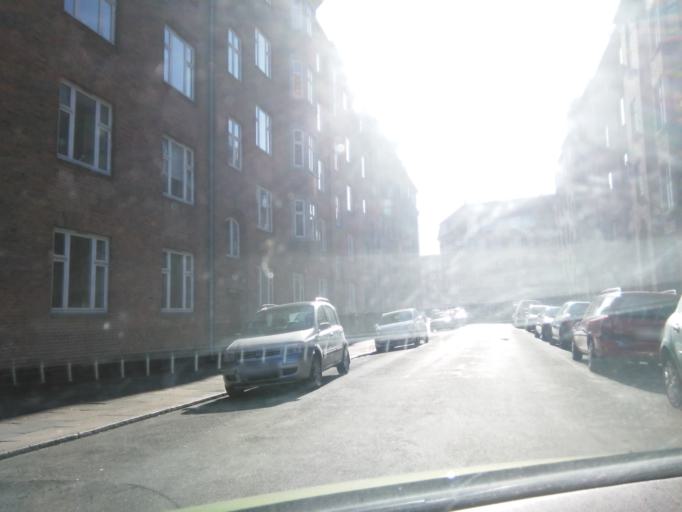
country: DK
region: Capital Region
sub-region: Kobenhavn
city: Christianshavn
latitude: 55.6651
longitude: 12.6030
